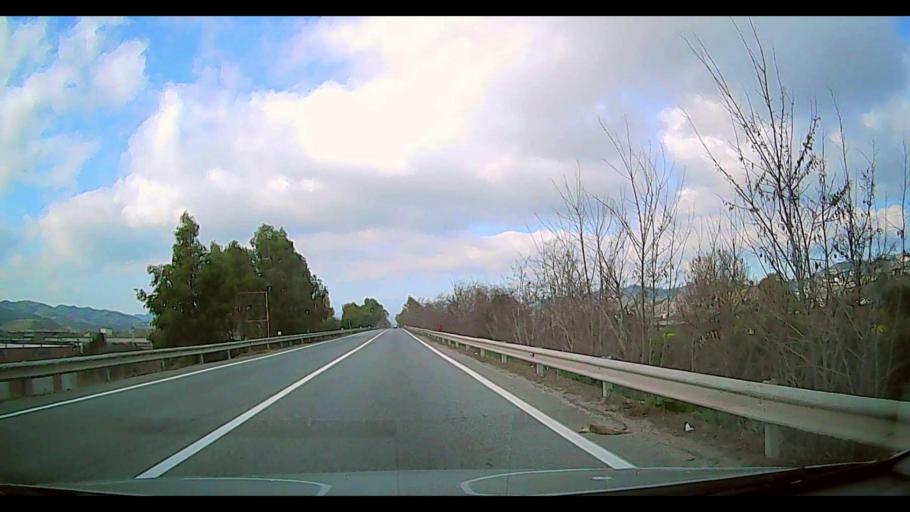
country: IT
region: Calabria
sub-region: Provincia di Crotone
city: Rocca di Neto
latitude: 39.1761
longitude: 17.0127
